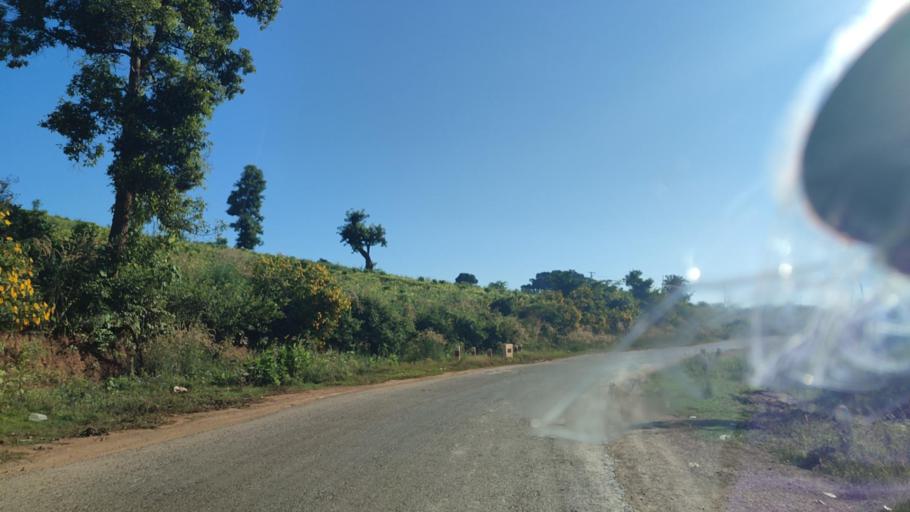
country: MM
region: Shan
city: Taunggyi
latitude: 20.9452
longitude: 97.6078
